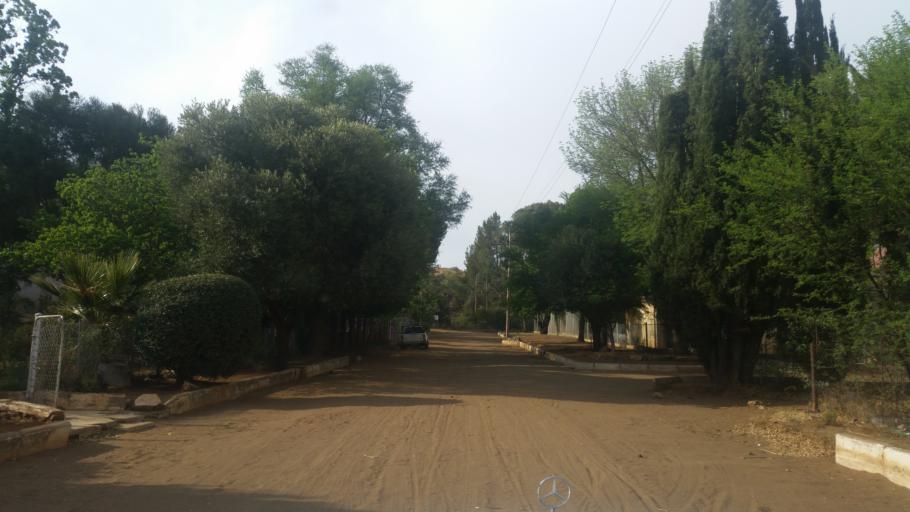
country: ZA
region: Orange Free State
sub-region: Xhariep District Municipality
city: Trompsburg
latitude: -30.4935
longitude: 25.9696
